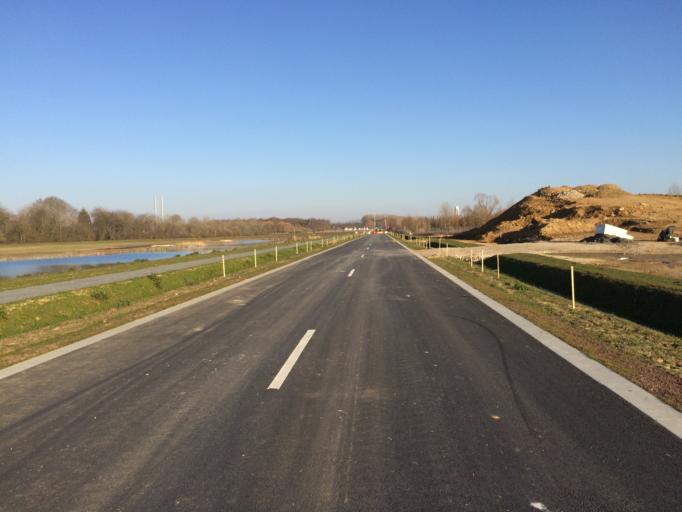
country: FR
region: Ile-de-France
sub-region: Departement de l'Essonne
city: Vauhallan
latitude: 48.7190
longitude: 2.1952
